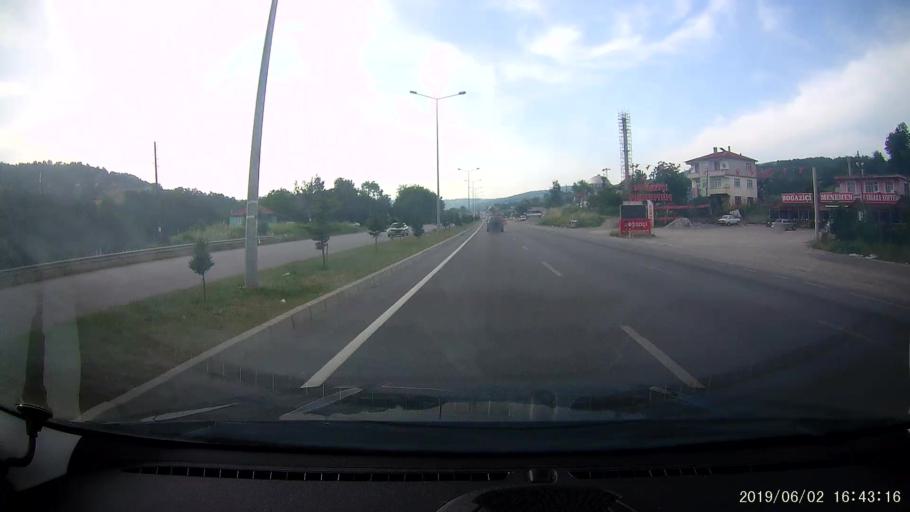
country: TR
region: Samsun
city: Kavak
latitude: 41.1325
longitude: 36.1306
